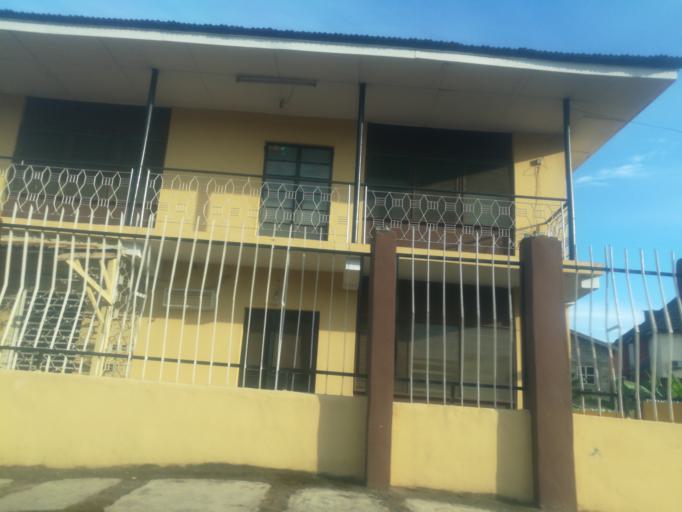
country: NG
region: Oyo
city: Ibadan
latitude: 7.3477
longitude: 3.8859
